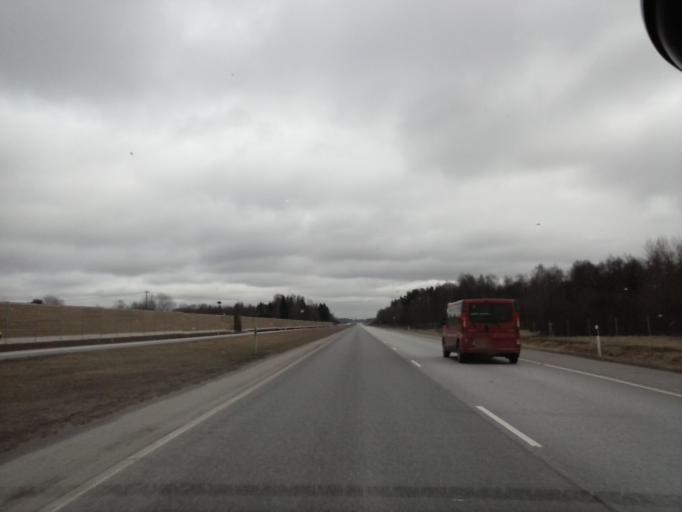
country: EE
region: Harju
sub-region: Rae vald
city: Jueri
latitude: 59.3257
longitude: 24.9196
